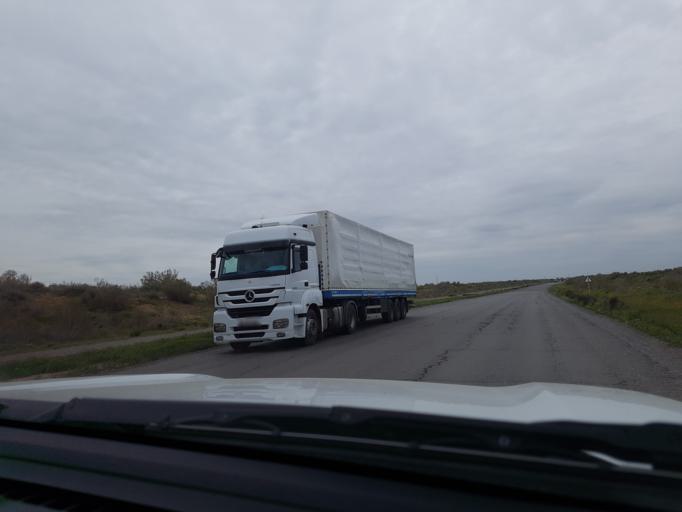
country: TM
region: Mary
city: Bayramaly
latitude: 37.8772
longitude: 62.6127
